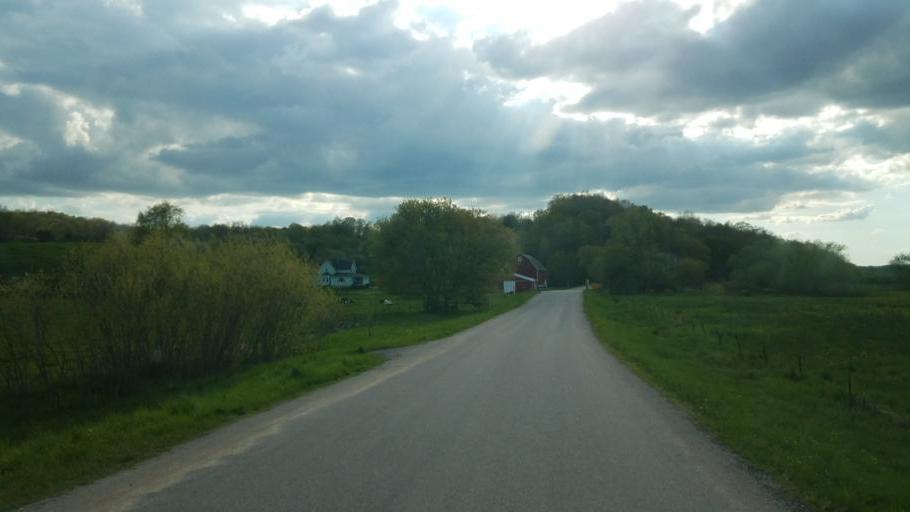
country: US
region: Wisconsin
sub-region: Vernon County
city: Hillsboro
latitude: 43.6545
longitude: -90.3646
